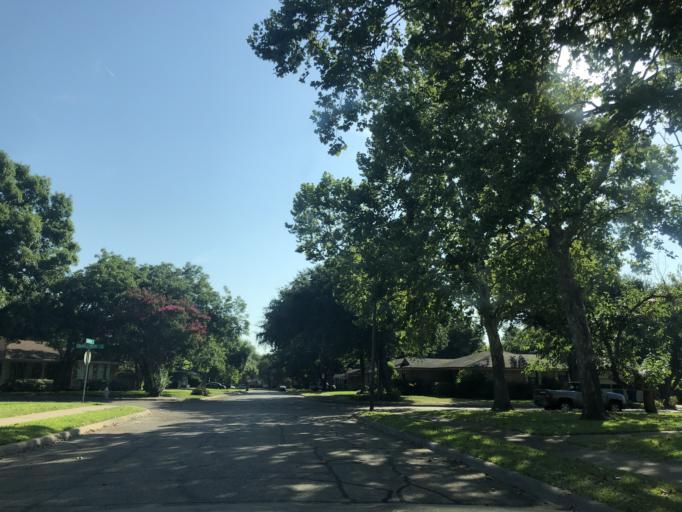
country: US
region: Texas
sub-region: Dallas County
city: Garland
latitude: 32.8697
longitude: -96.6467
